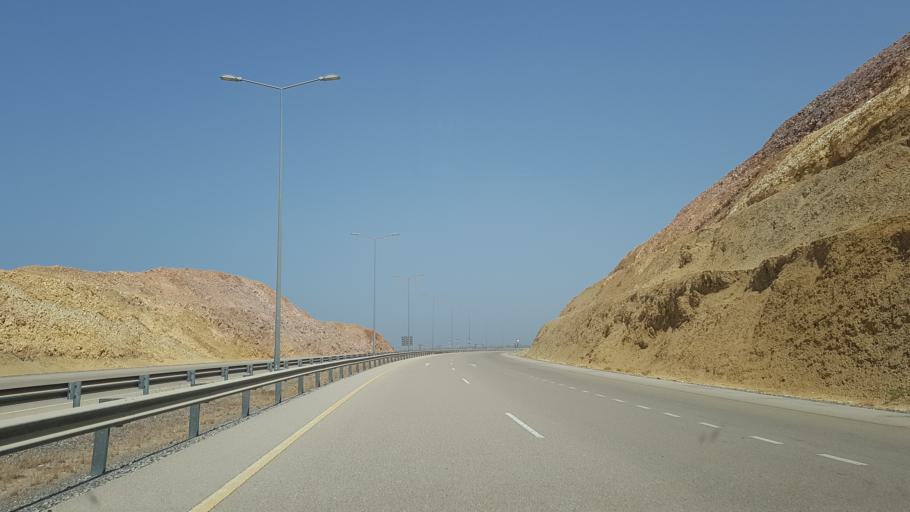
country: OM
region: Muhafazat Masqat
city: Muscat
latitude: 23.2132
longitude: 58.9310
